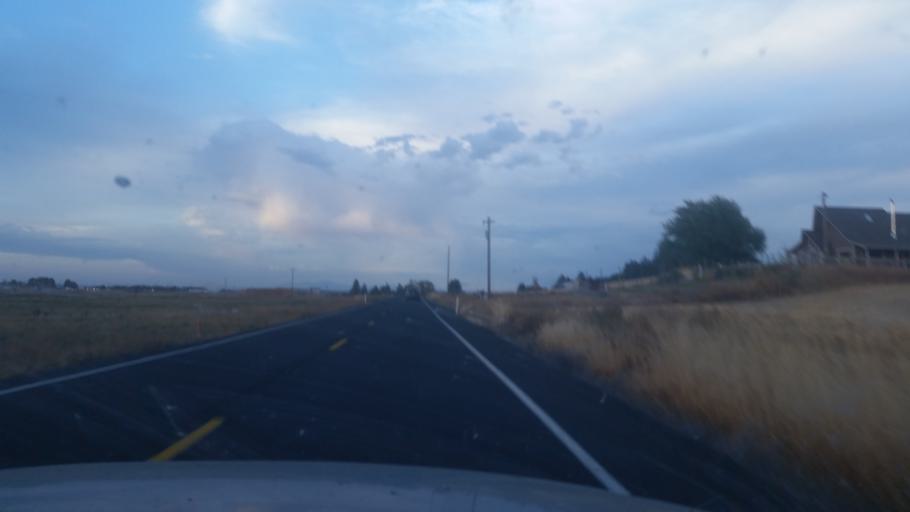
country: US
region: Washington
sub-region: Spokane County
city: Airway Heights
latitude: 47.5709
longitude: -117.5839
